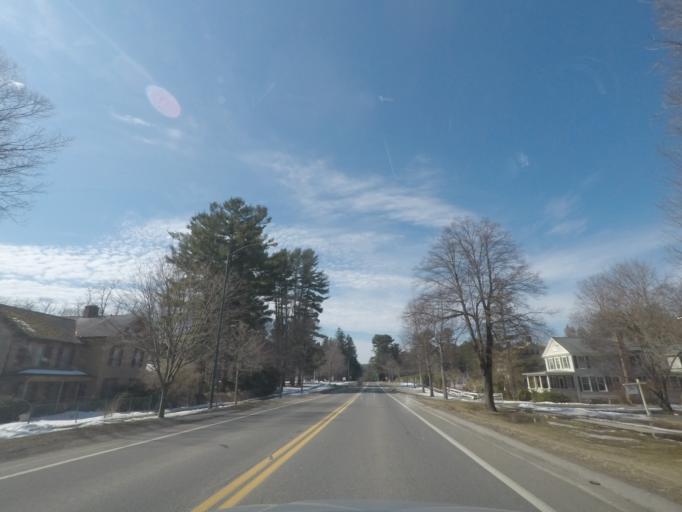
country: US
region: Massachusetts
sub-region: Berkshire County
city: Stockbridge
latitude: 42.2834
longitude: -73.3176
